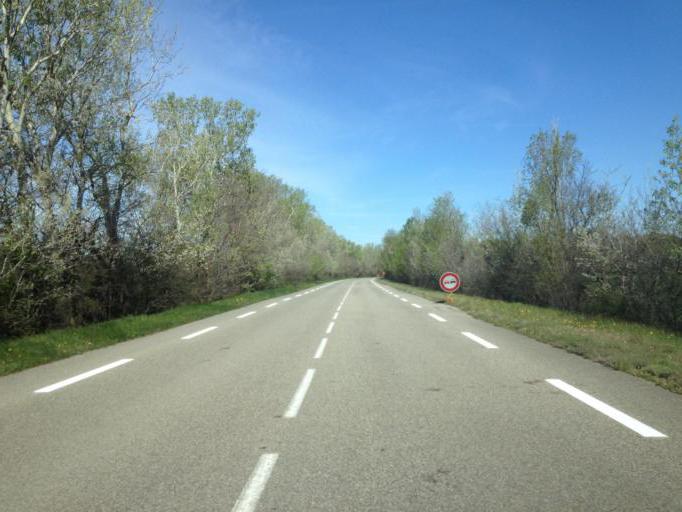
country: FR
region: Provence-Alpes-Cote d'Azur
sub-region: Departement du Vaucluse
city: Caderousse
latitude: 44.1145
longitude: 4.7236
